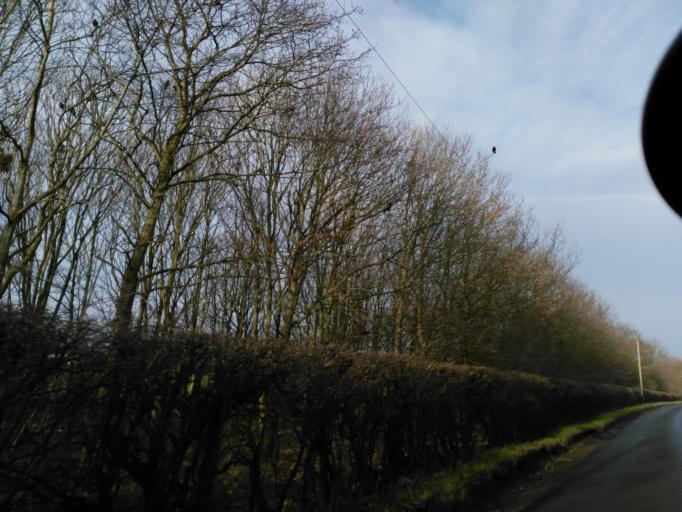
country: GB
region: England
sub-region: Wiltshire
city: Marston
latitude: 51.3235
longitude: -2.0583
